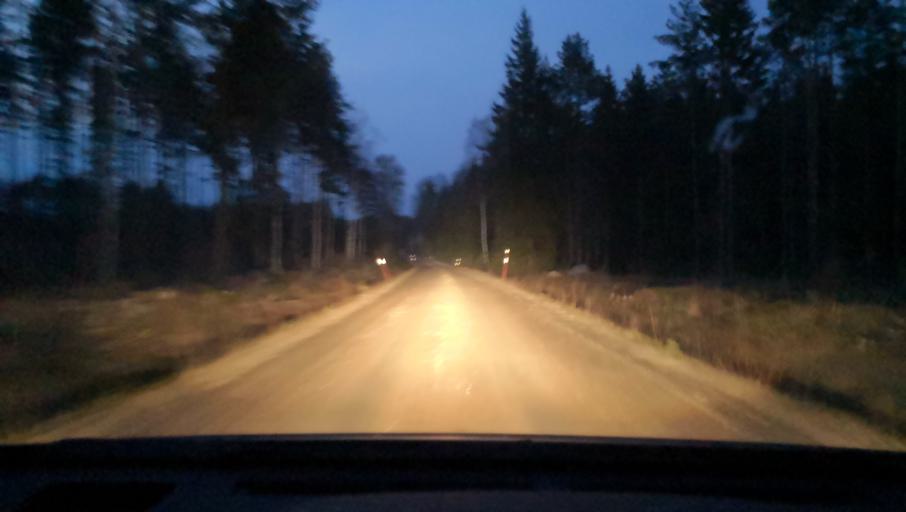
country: SE
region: OErebro
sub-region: Lindesbergs Kommun
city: Frovi
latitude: 59.6092
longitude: 15.4774
